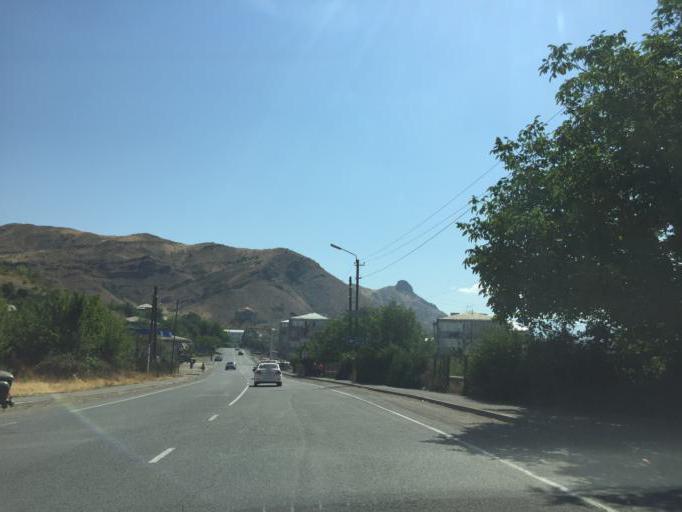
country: AM
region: Vayots' Dzori Marz
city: Vayk'
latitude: 39.6952
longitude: 45.4534
